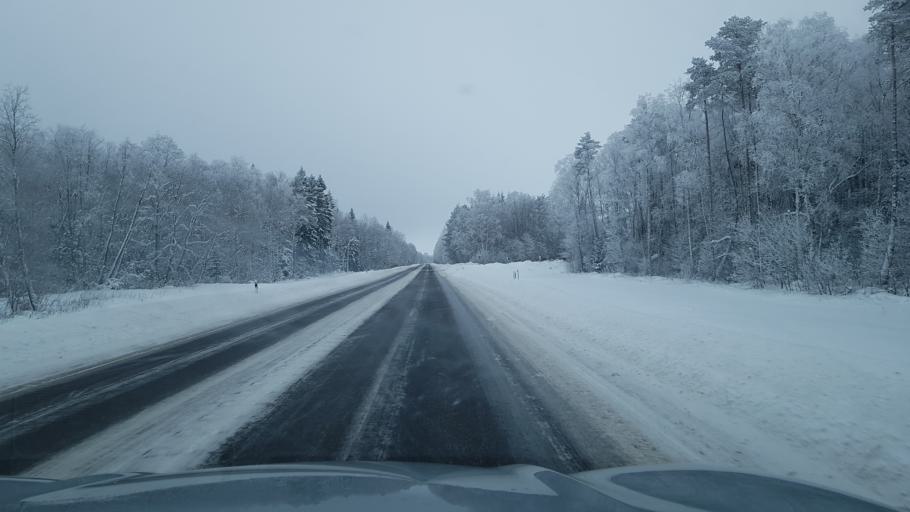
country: EE
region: Ida-Virumaa
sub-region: Johvi vald
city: Johvi
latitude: 59.2948
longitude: 27.3985
